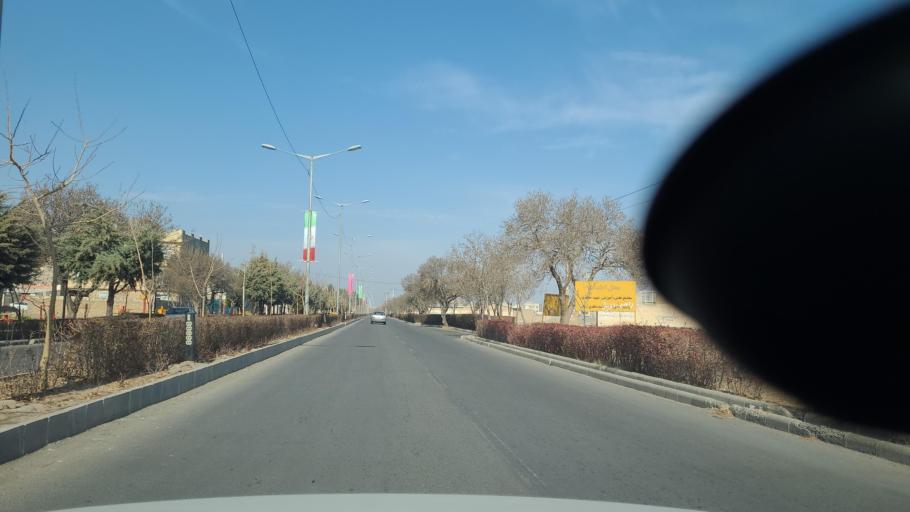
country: IR
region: Razavi Khorasan
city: Fariman
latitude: 35.6862
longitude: 59.8436
